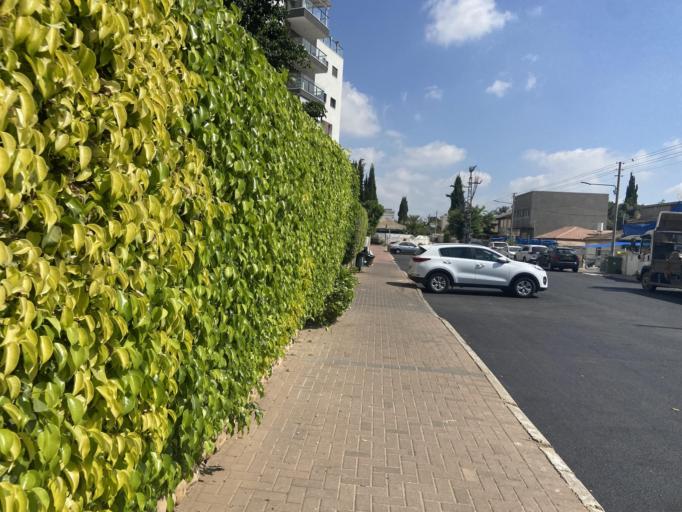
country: IL
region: Central District
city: Yehud
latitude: 32.0360
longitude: 34.8907
